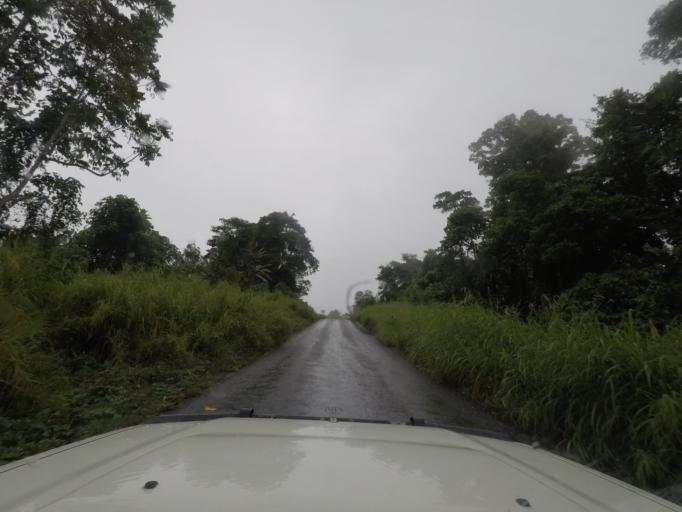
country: PG
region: Madang
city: Madang
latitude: -5.4438
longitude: 145.5190
